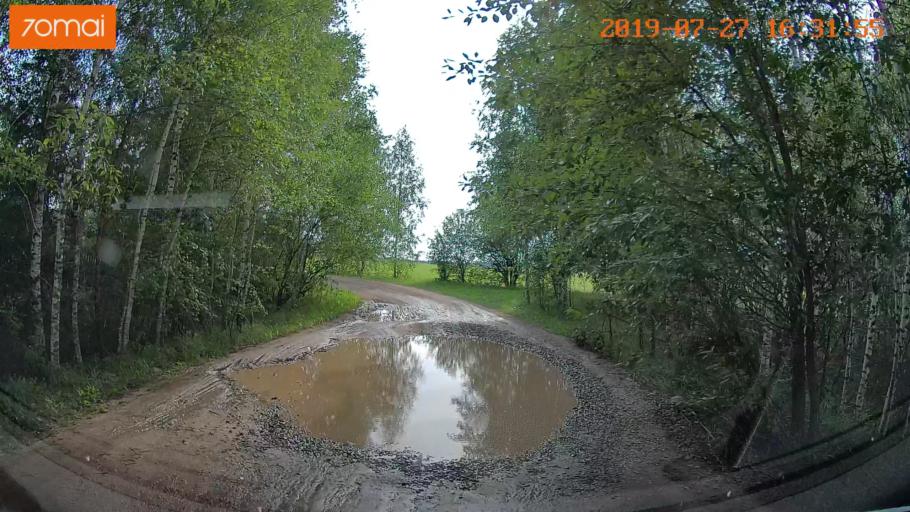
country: RU
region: Ivanovo
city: Novo-Talitsy
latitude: 57.0904
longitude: 40.8519
